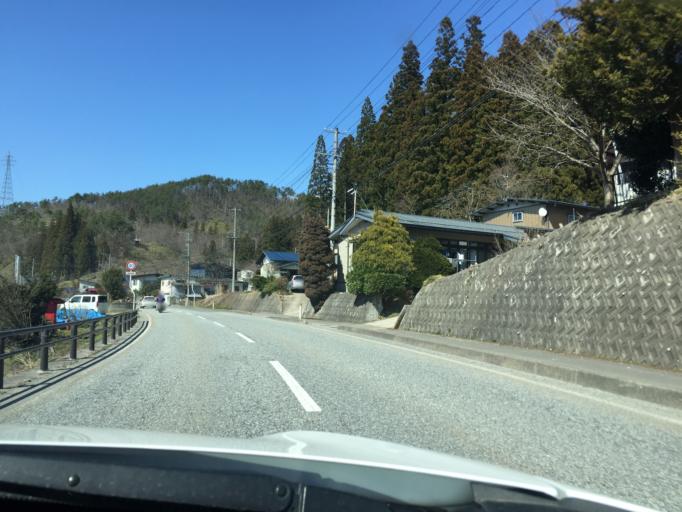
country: JP
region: Yamagata
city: Nagai
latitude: 38.2014
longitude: 140.1041
